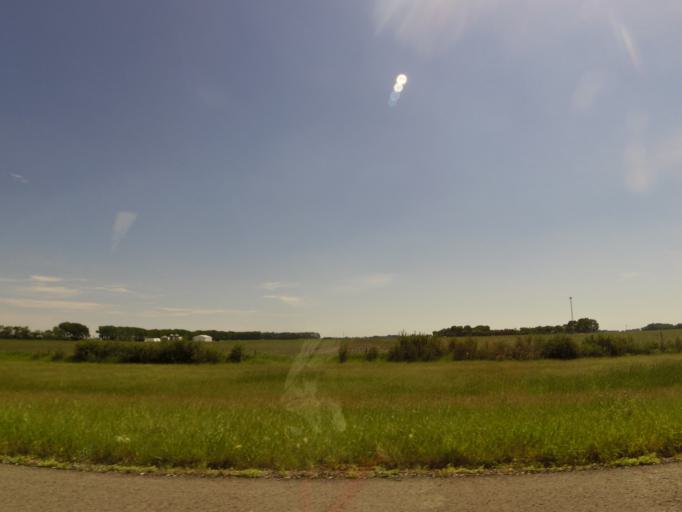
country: US
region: North Dakota
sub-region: Grand Forks County
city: Grand Forks
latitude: 47.7620
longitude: -97.0775
